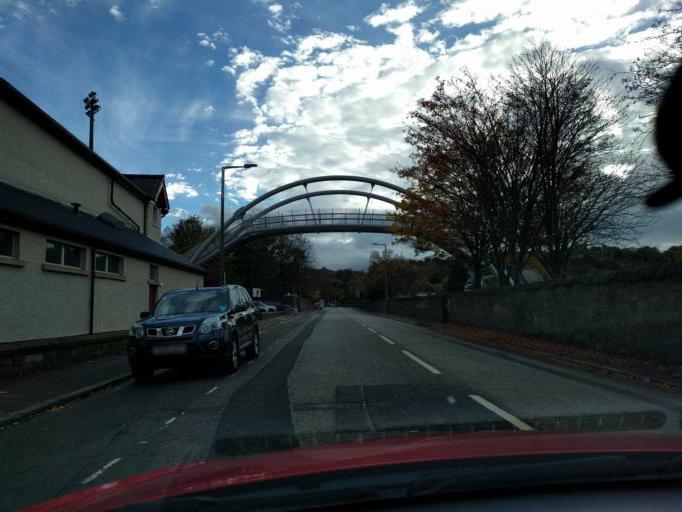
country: GB
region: Scotland
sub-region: Edinburgh
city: Edinburgh
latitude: 55.9279
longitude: -3.2238
